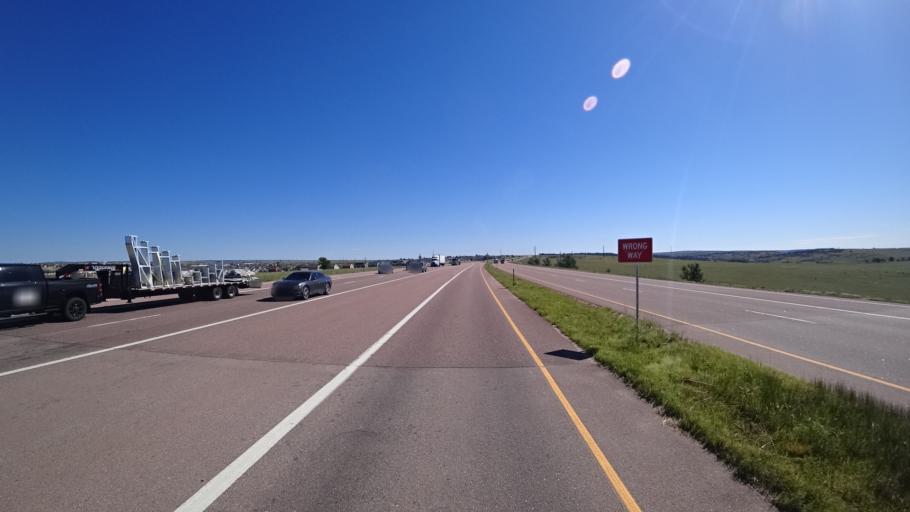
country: US
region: Colorado
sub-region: El Paso County
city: Cimarron Hills
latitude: 38.8527
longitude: -104.6813
